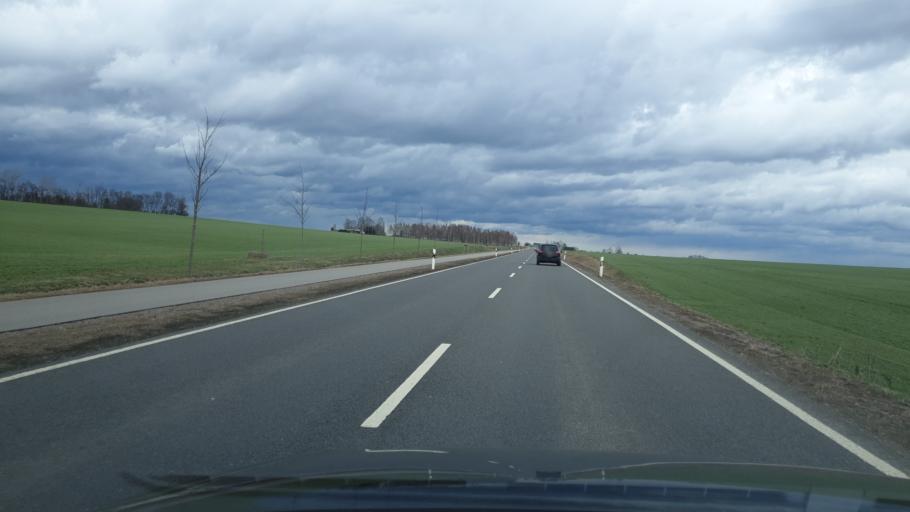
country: DE
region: Saxony
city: Claussnitz
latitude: 50.9499
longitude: 12.9094
